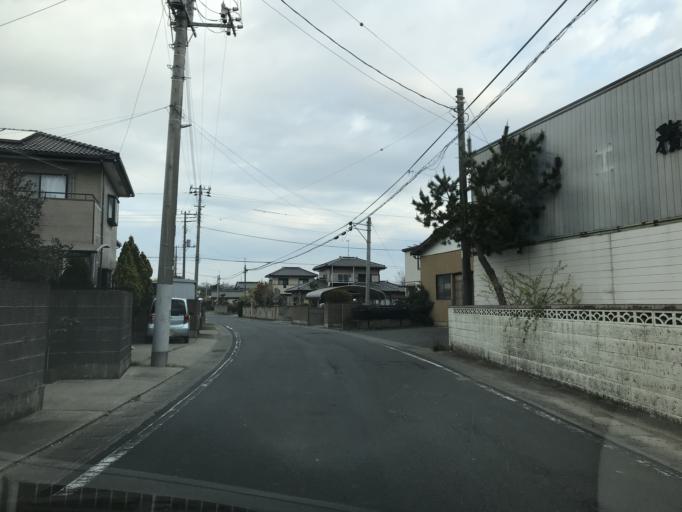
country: JP
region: Ibaraki
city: Kashima-shi
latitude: 35.9134
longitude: 140.6271
